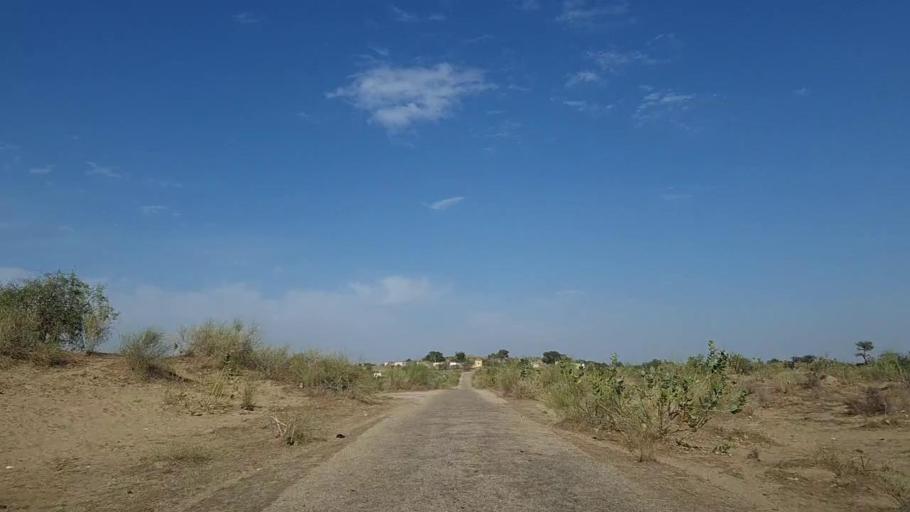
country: PK
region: Sindh
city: Naukot
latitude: 24.8495
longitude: 69.5599
